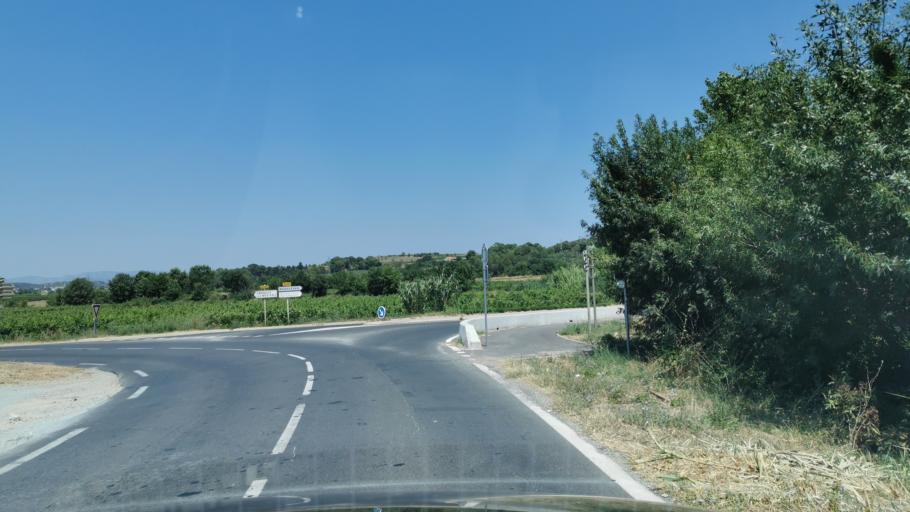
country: FR
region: Languedoc-Roussillon
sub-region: Departement de l'Herault
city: Maureilhan
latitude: 43.3639
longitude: 3.1212
